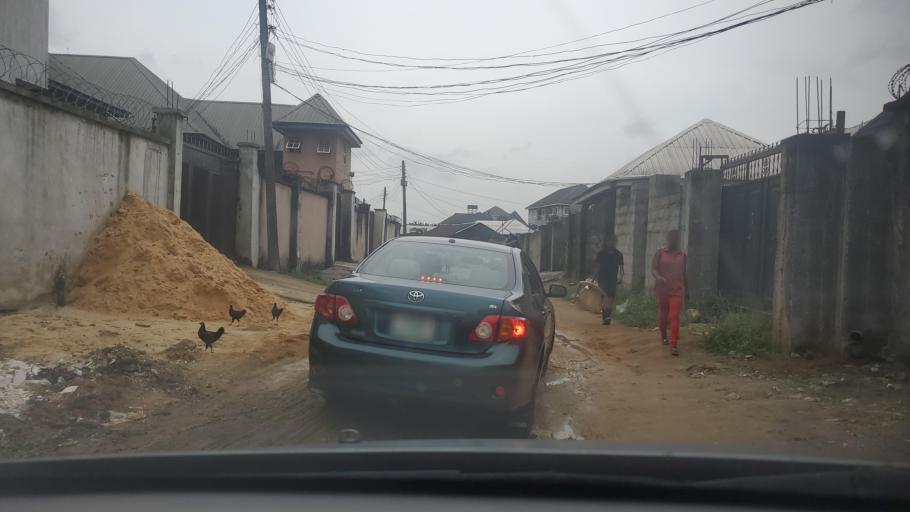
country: NG
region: Rivers
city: Port Harcourt
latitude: 4.8442
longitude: 7.0012
